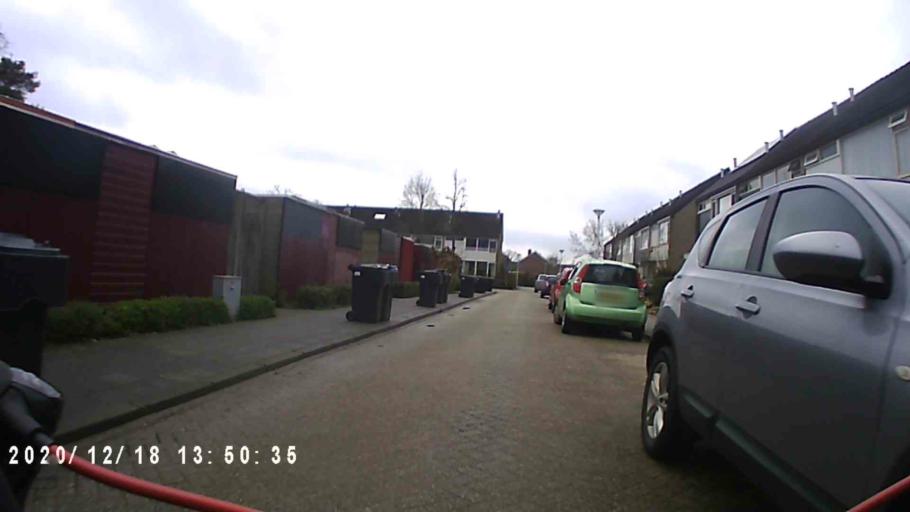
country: NL
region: Groningen
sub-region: Gemeente Bedum
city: Bedum
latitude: 53.2998
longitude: 6.6068
